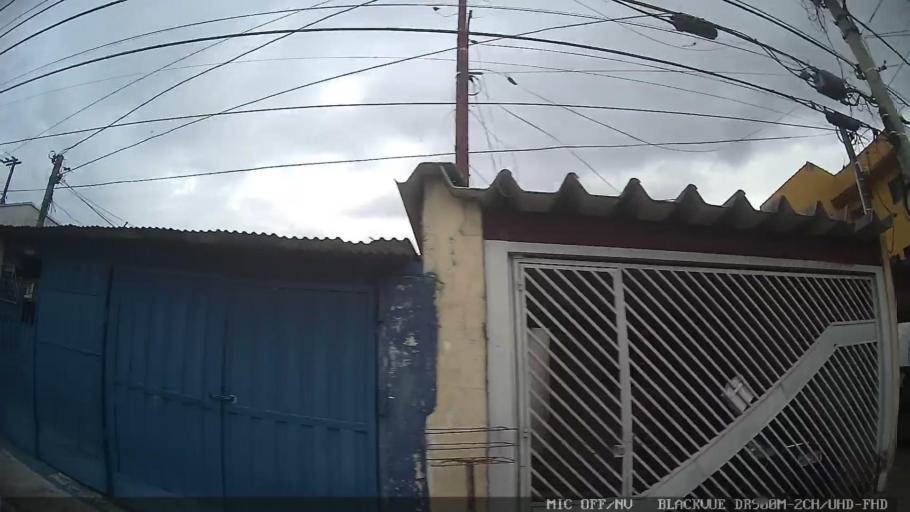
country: BR
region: Sao Paulo
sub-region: Mogi das Cruzes
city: Mogi das Cruzes
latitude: -23.5381
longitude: -46.1869
